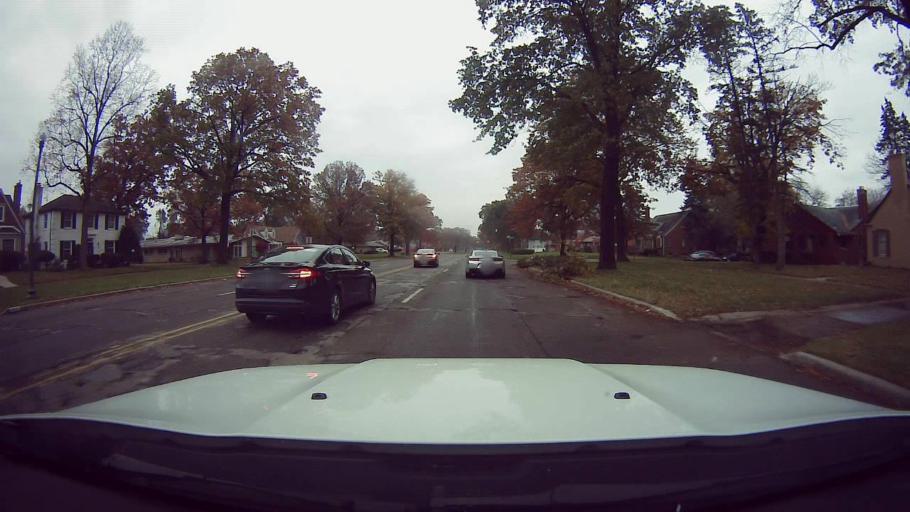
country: US
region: Michigan
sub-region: Oakland County
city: Oak Park
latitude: 42.4349
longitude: -83.1644
